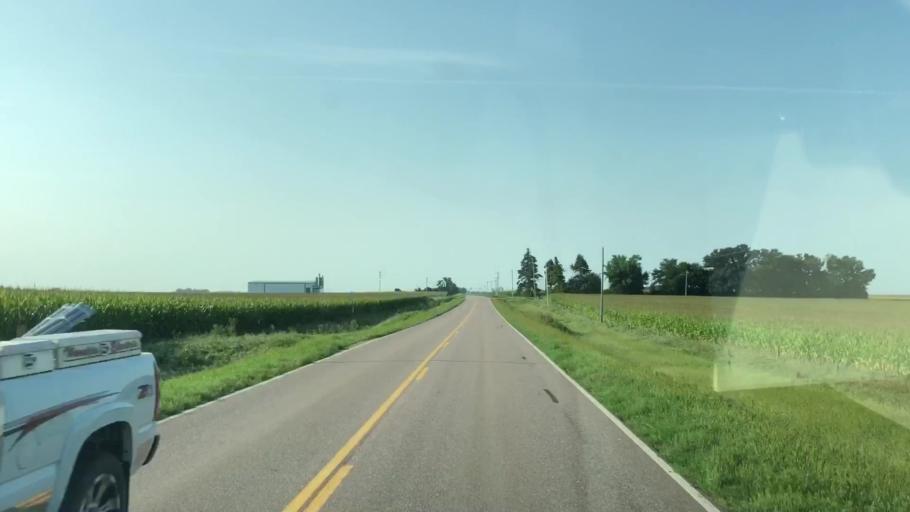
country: US
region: Iowa
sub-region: Lyon County
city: George
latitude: 43.2320
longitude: -96.0007
